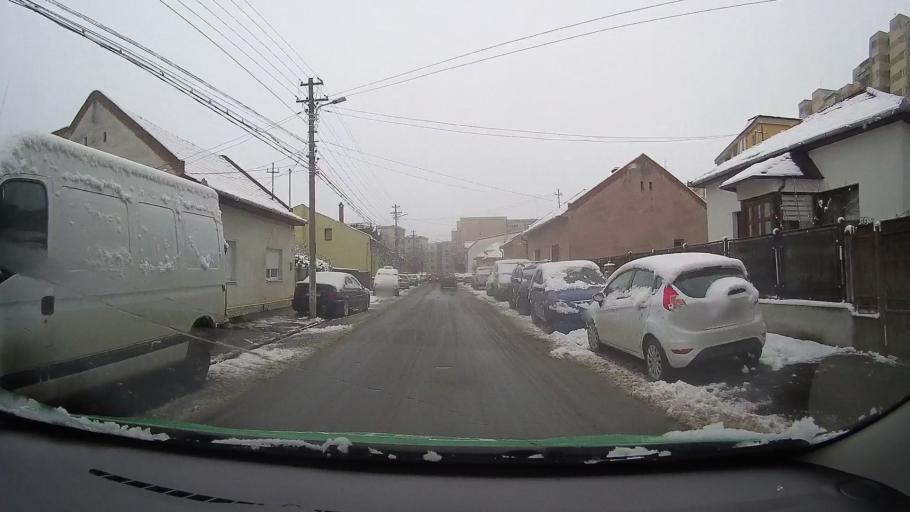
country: RO
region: Hunedoara
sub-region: Municipiul Deva
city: Deva
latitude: 45.8748
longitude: 22.9097
